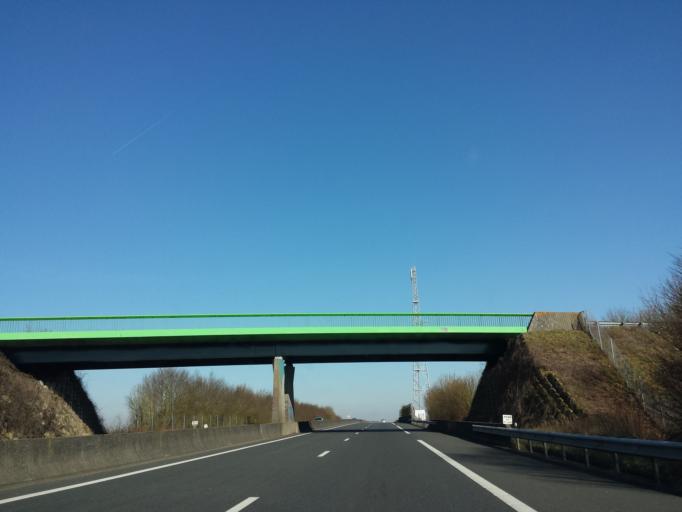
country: FR
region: Picardie
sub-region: Departement de l'Oise
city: Crevecoeur-le-Grand
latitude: 49.5559
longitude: 2.1922
